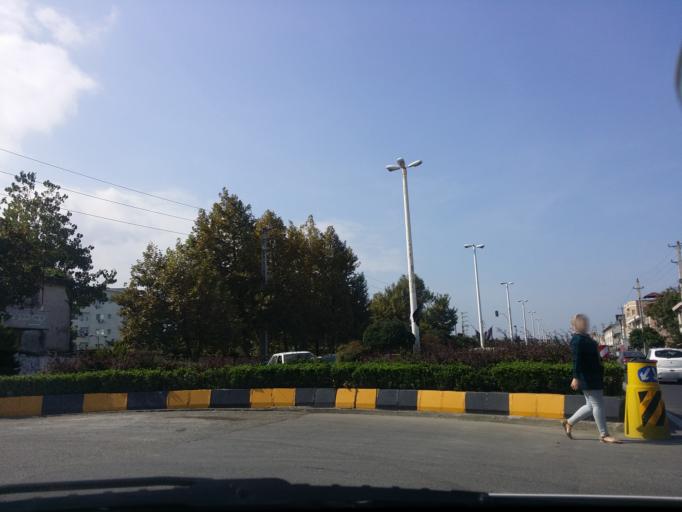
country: IR
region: Mazandaran
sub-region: Nowshahr
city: Nowshahr
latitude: 36.6570
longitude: 51.4852
